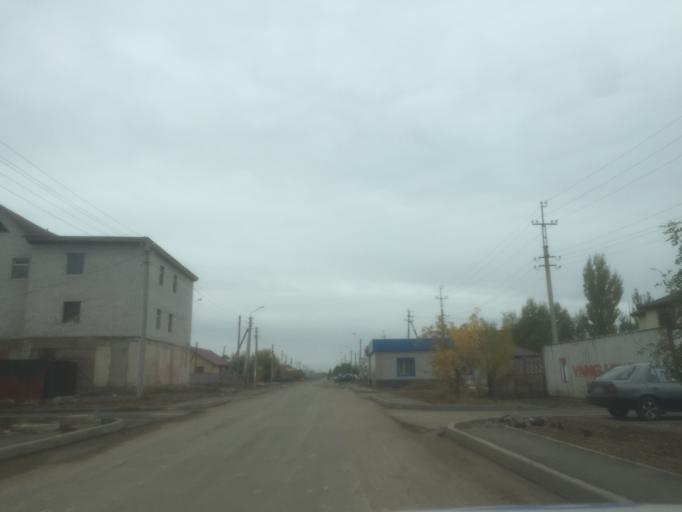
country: KZ
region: Astana Qalasy
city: Astana
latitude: 51.1938
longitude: 71.3372
